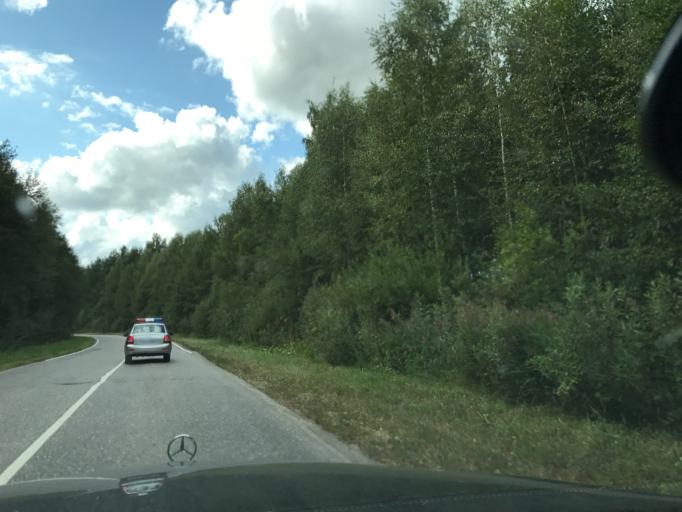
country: RU
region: Vladimir
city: Vorsha
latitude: 56.0101
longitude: 40.1177
